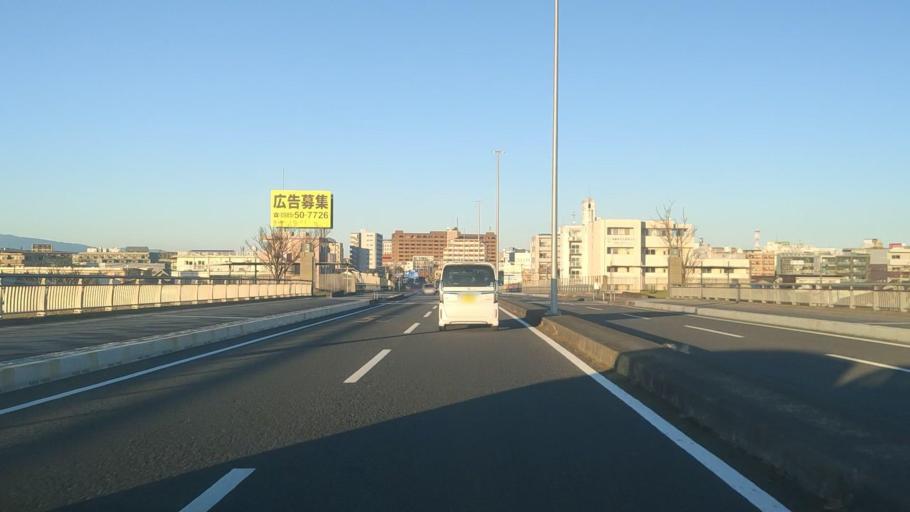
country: JP
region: Miyazaki
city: Miyazaki-shi
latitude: 31.9096
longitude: 131.4123
